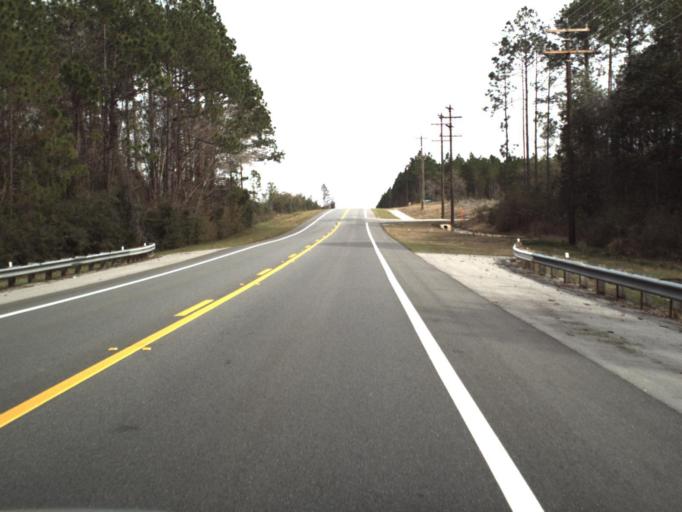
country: US
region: Florida
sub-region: Bay County
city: Callaway
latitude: 30.1501
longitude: -85.4729
